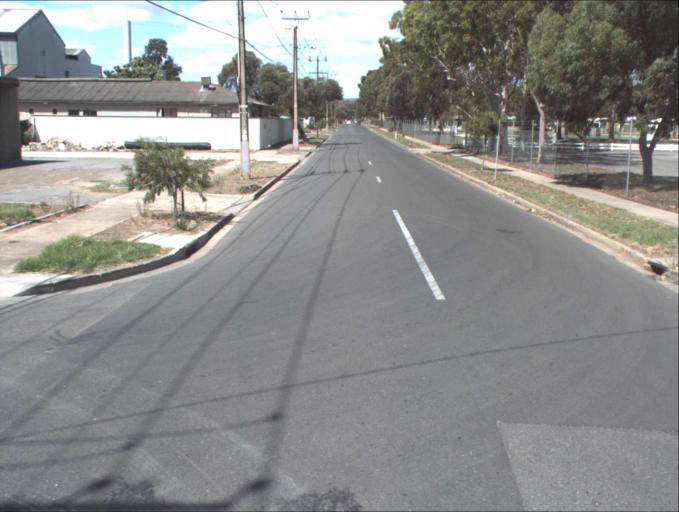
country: AU
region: South Australia
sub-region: Port Adelaide Enfield
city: Blair Athol
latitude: -34.8544
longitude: 138.5851
